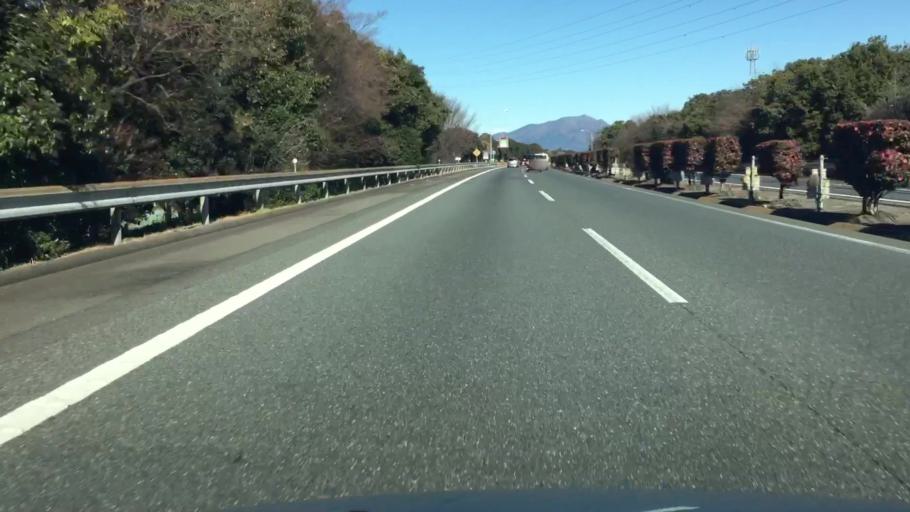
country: JP
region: Gunma
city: Kanekomachi
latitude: 36.4306
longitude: 139.0150
